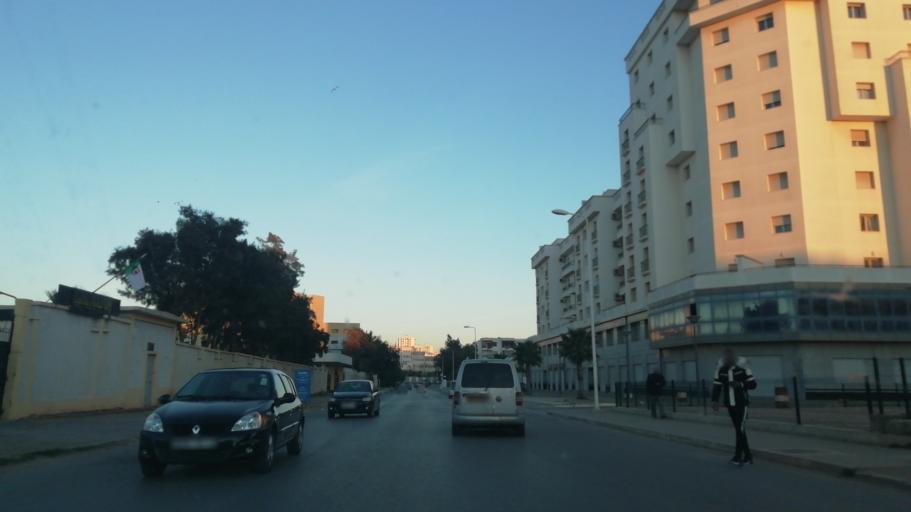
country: DZ
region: Oran
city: Bir el Djir
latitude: 35.6984
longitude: -0.5900
